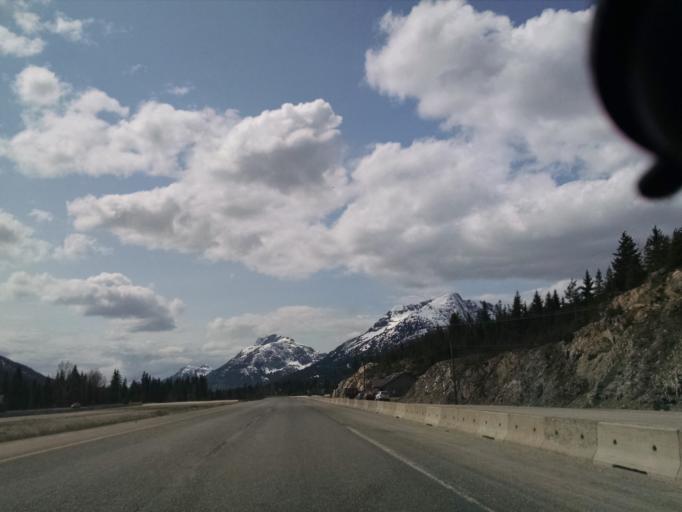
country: CA
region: British Columbia
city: Hope
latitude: 49.6314
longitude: -121.0149
